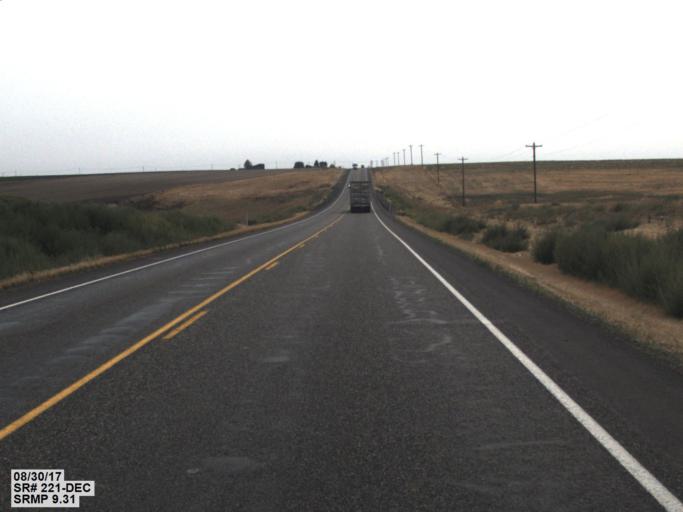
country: US
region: Oregon
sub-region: Morrow County
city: Irrigon
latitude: 46.0700
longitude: -119.6021
